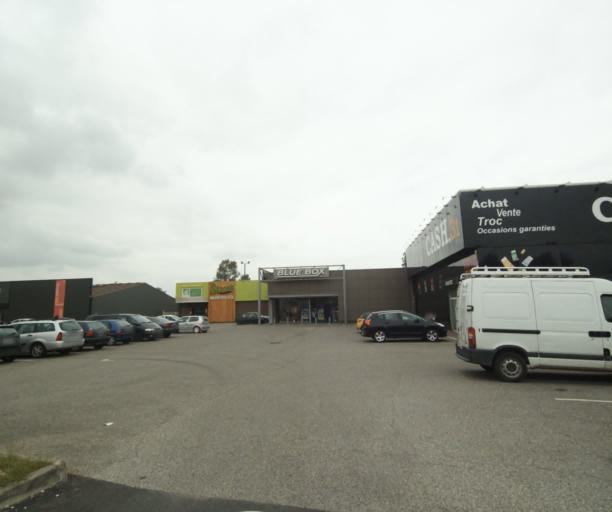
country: FR
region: Midi-Pyrenees
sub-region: Departement du Tarn-et-Garonne
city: Montauban
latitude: 44.0012
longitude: 1.3547
